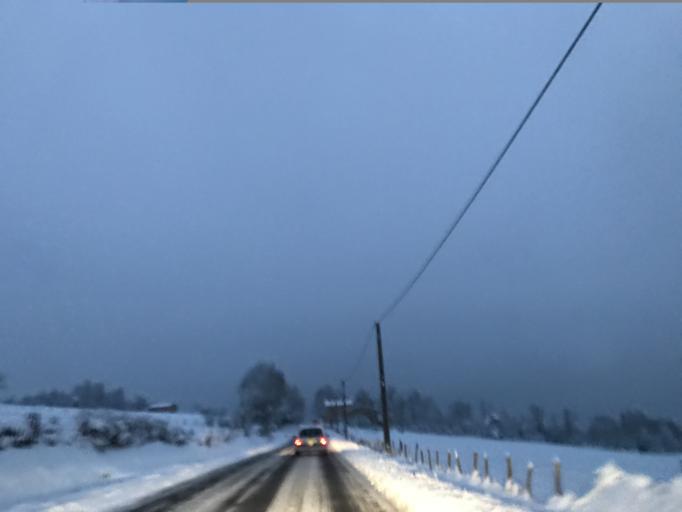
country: FR
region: Auvergne
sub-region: Departement du Puy-de-Dome
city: Courpiere
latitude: 45.7189
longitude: 3.5885
